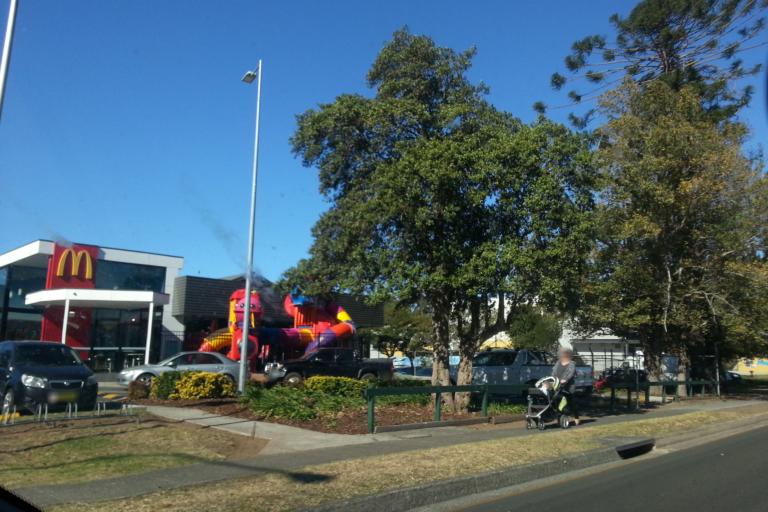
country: AU
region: New South Wales
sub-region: Wollongong
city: Dapto
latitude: -34.4955
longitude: 150.7932
